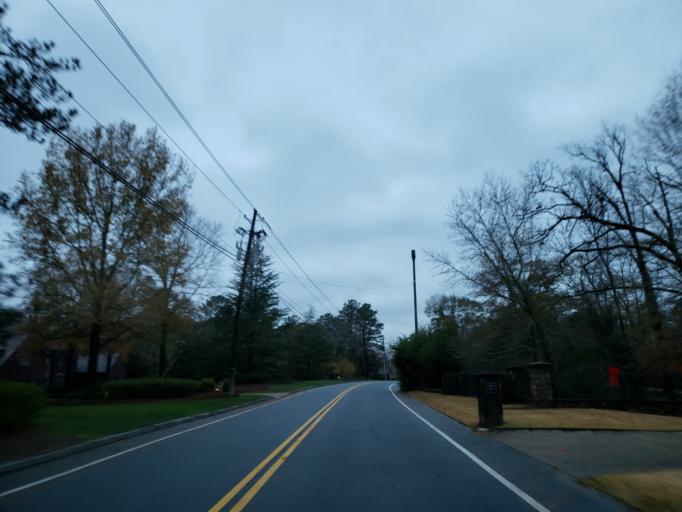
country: US
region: Georgia
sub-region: Cobb County
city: Vinings
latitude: 33.8806
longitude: -84.4223
